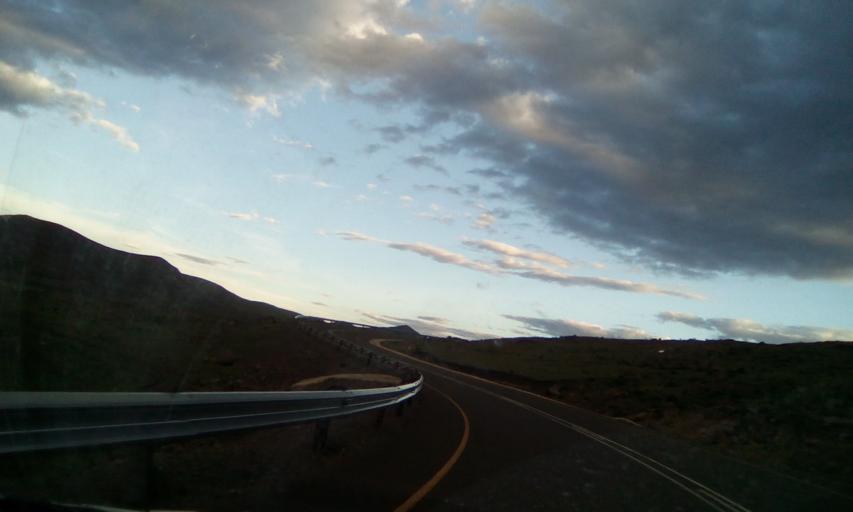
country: LS
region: Maseru
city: Nako
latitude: -29.8161
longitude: 28.0351
